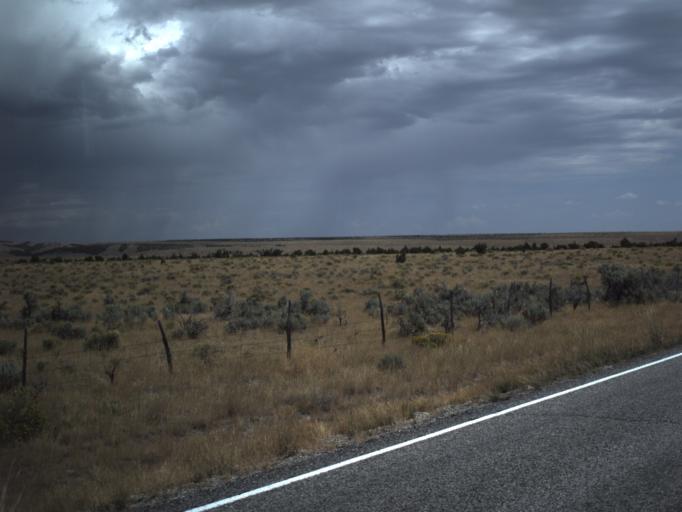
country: US
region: Idaho
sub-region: Cassia County
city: Burley
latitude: 41.8173
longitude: -113.2612
